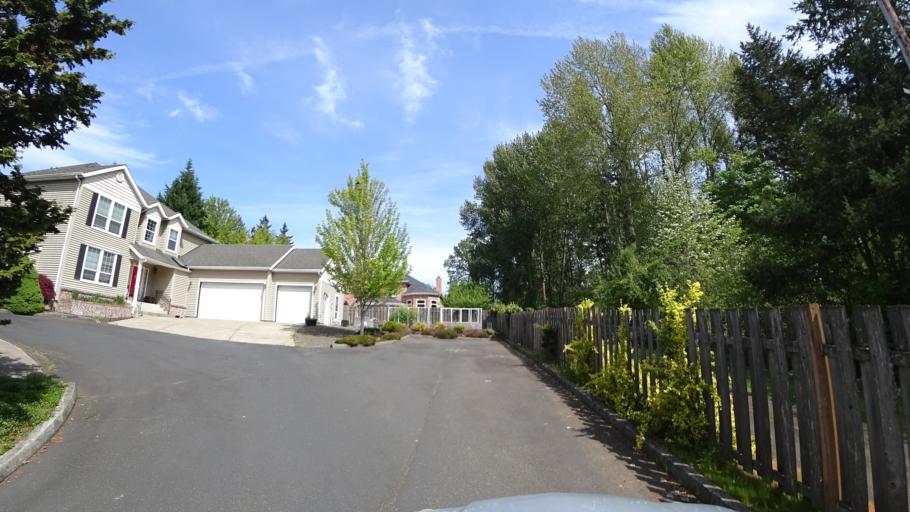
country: US
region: Oregon
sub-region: Washington County
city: Hillsboro
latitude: 45.5246
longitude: -122.9339
